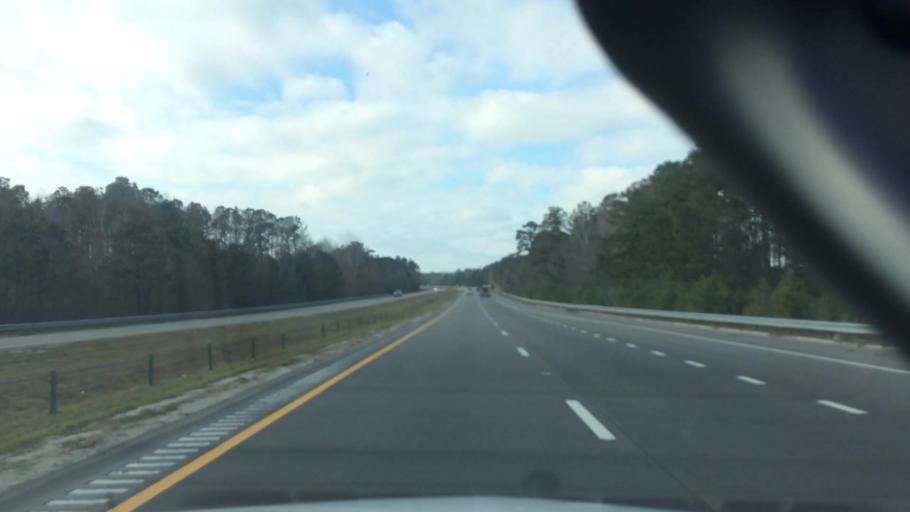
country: US
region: North Carolina
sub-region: New Hanover County
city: Wrightsboro
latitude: 34.3179
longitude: -77.9252
